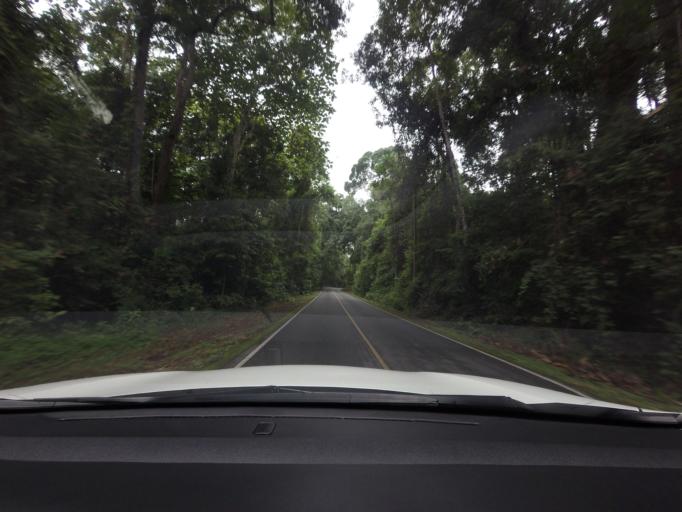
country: TH
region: Nakhon Ratchasima
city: Pak Chong
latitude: 14.4577
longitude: 101.3738
